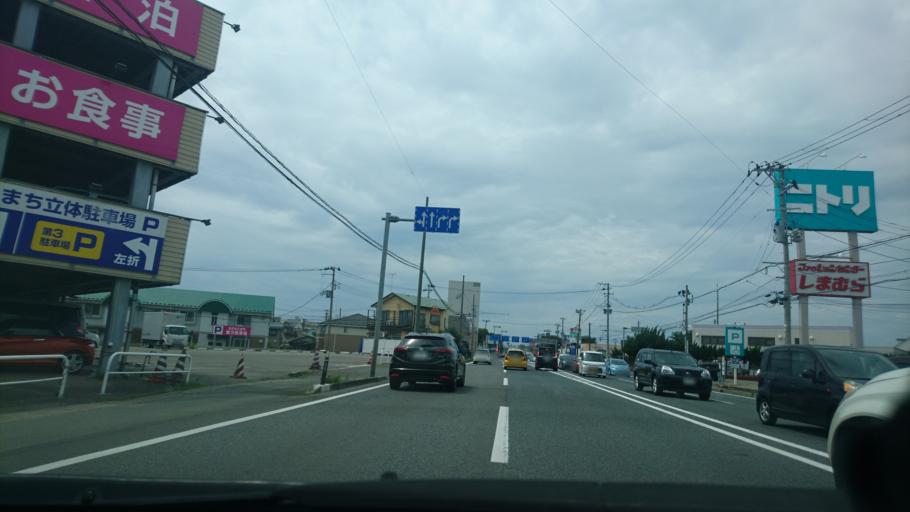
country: JP
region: Akita
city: Akita Shi
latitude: 39.7020
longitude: 140.1077
